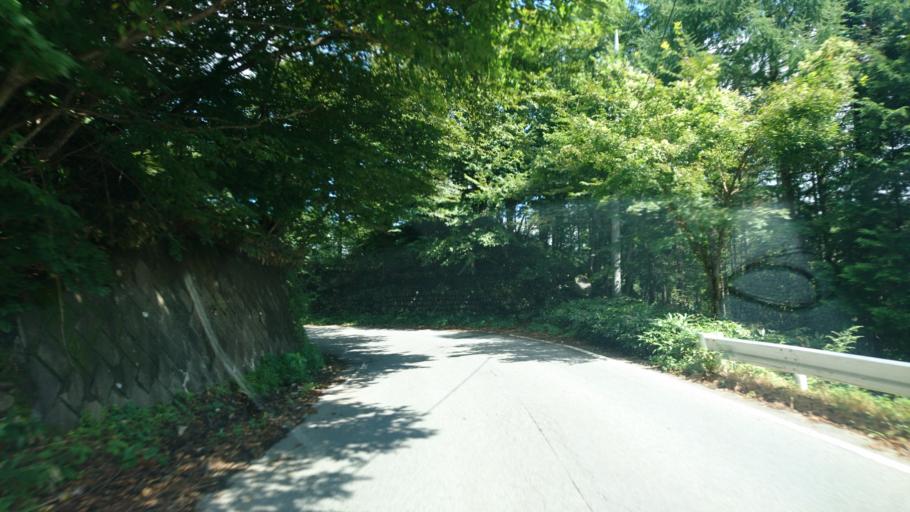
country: JP
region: Gunma
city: Omamacho-omama
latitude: 36.5768
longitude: 139.2346
